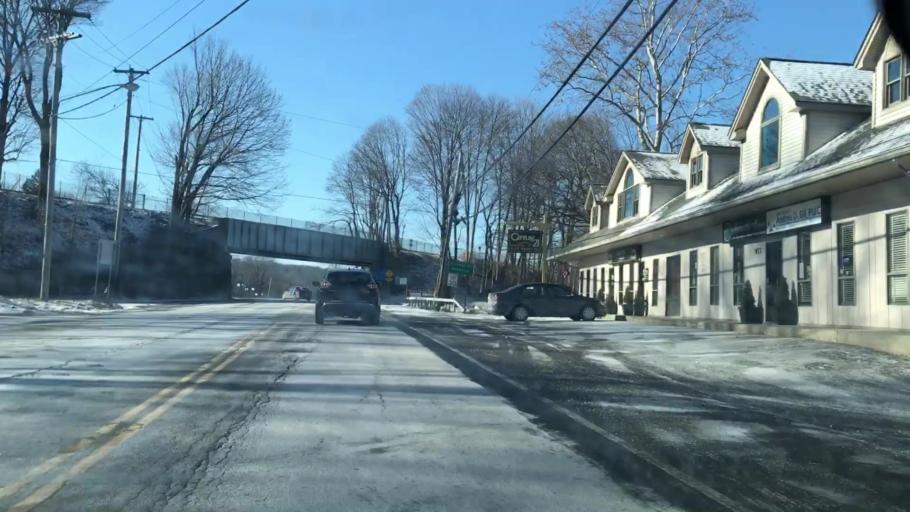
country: US
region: New York
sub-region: Putnam County
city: Brewster
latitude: 41.3972
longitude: -73.6033
